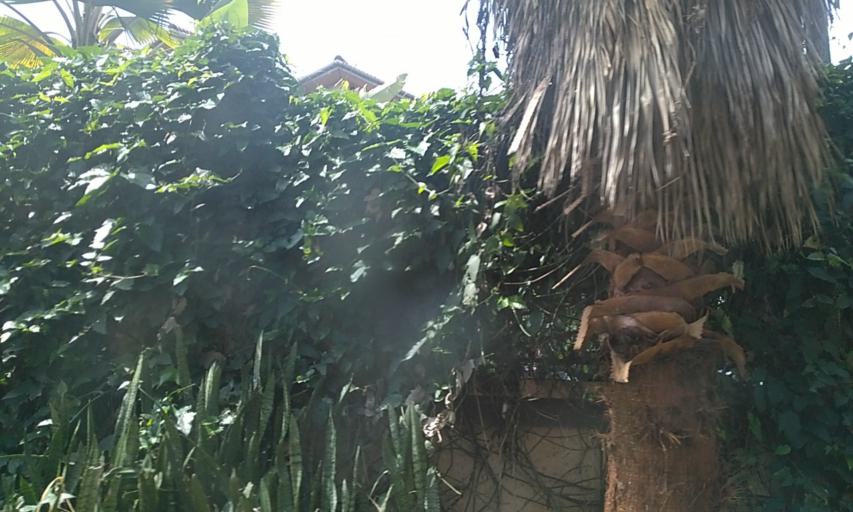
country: UG
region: Central Region
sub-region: Kampala District
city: Kampala
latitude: 0.3263
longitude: 32.5987
